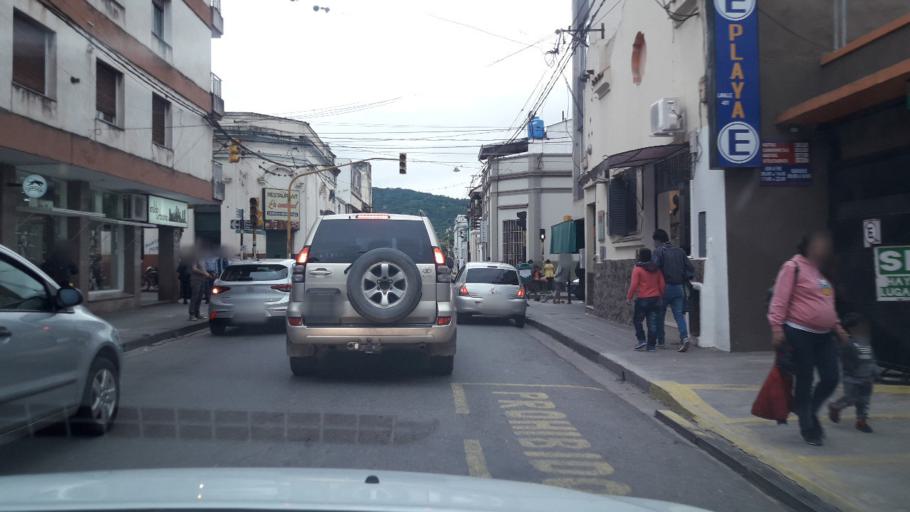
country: AR
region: Jujuy
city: San Salvador de Jujuy
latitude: -24.1832
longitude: -65.3029
